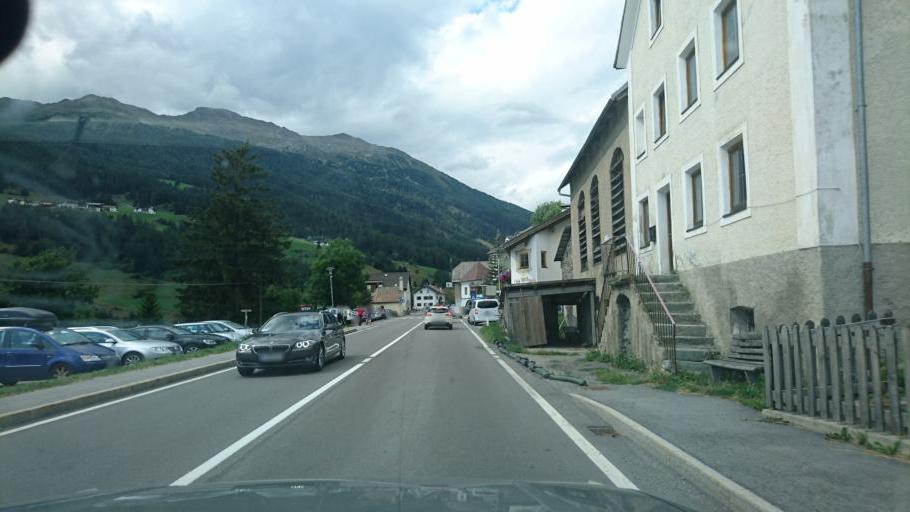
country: IT
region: Trentino-Alto Adige
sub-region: Bolzano
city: Curon Venosta
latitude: 46.7594
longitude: 10.5370
